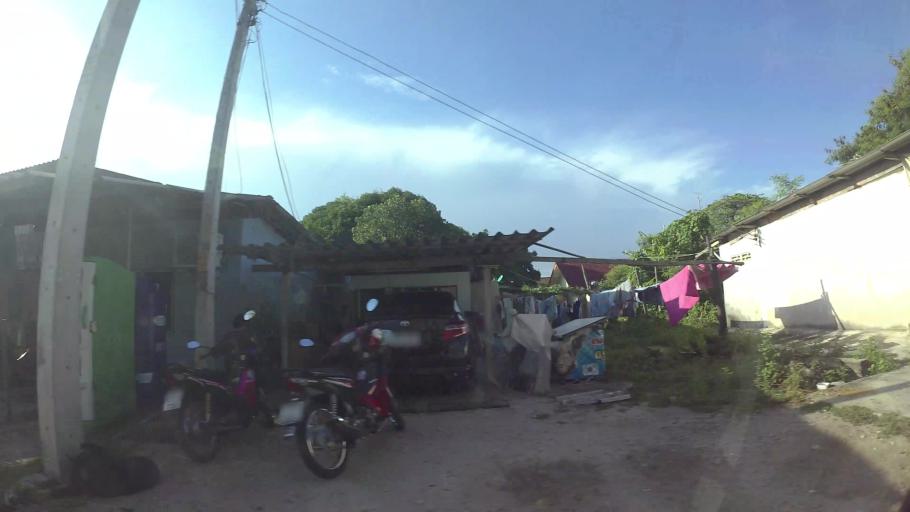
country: TH
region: Rayong
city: Rayong
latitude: 12.6905
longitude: 101.2781
